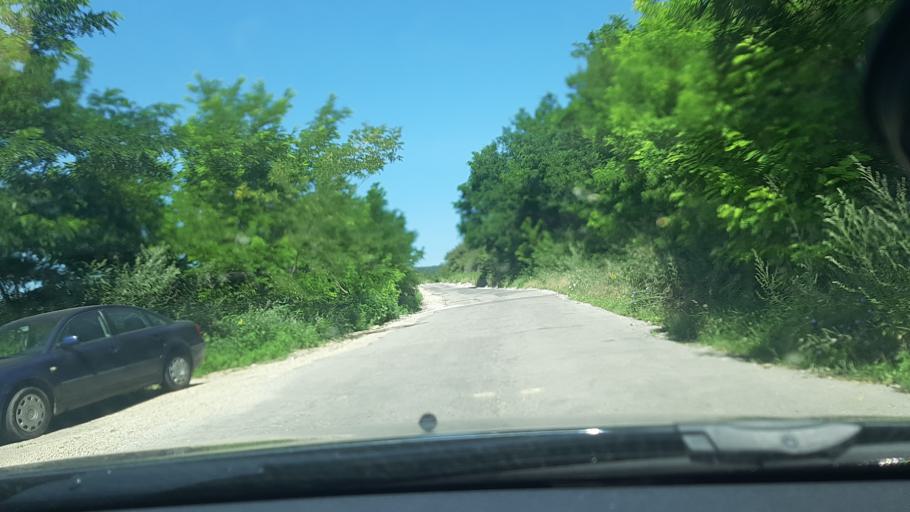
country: RO
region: Hunedoara
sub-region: Comuna Teliucu Inferior
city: Teliucu Inferior
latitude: 45.6889
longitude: 22.8760
